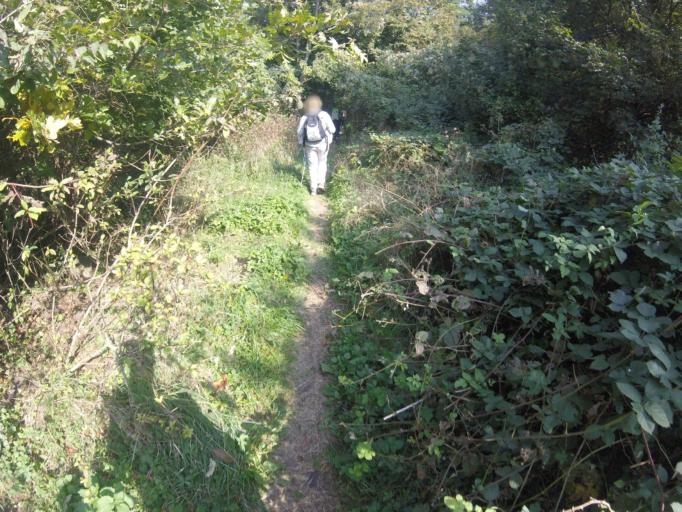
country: HU
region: Komarom-Esztergom
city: Kesztolc
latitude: 47.7353
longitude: 18.8433
